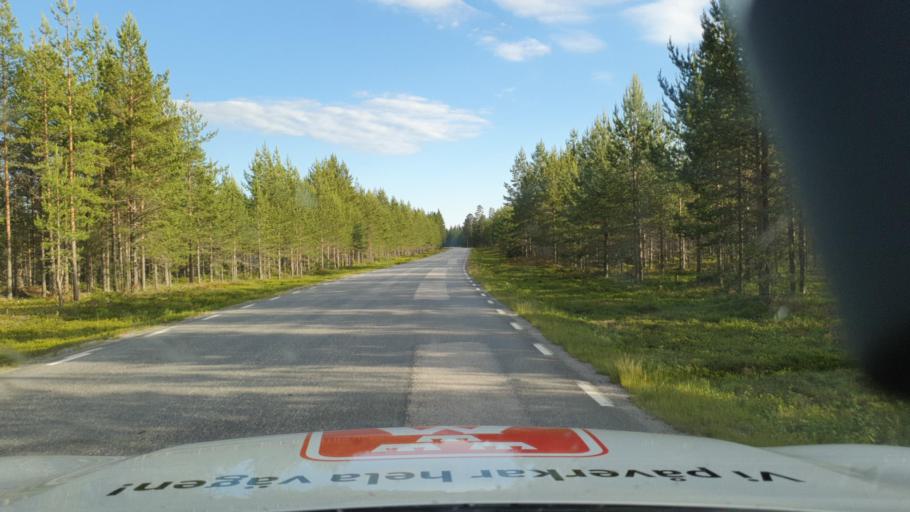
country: SE
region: Vaesterbotten
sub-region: Umea Kommun
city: Roback
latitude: 63.8845
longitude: 20.1516
